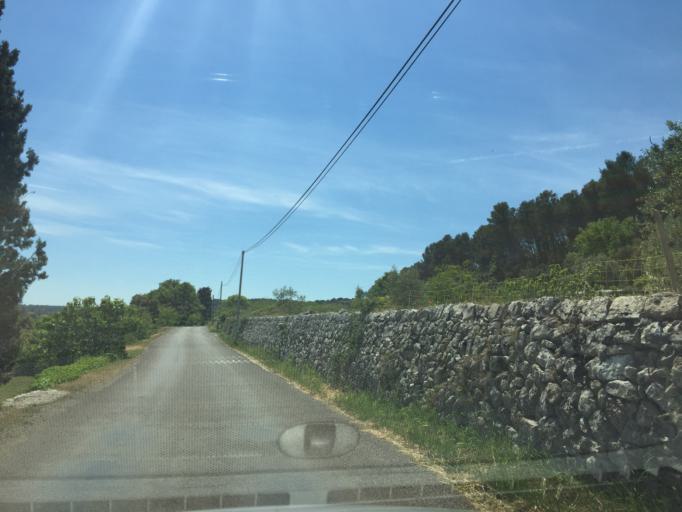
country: FR
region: Provence-Alpes-Cote d'Azur
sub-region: Departement du Var
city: Lorgues
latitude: 43.4812
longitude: 6.3663
